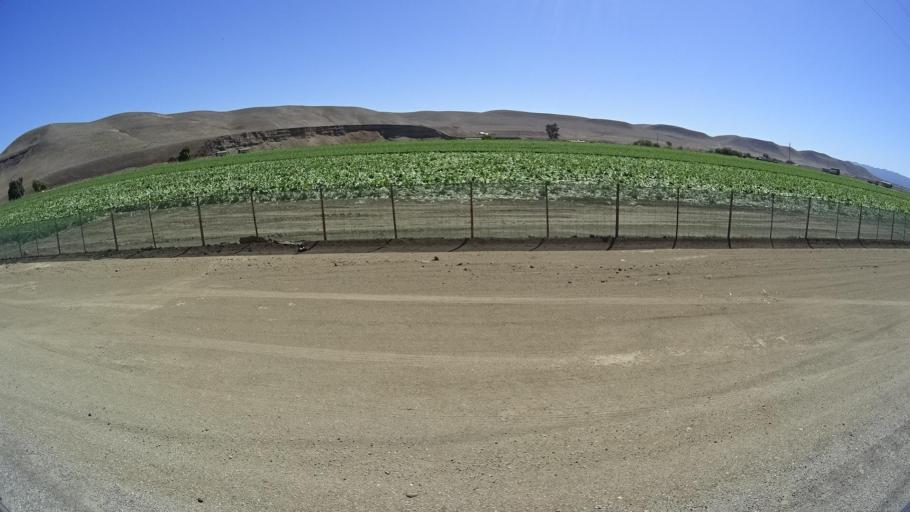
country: US
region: California
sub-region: Monterey County
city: King City
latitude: 36.2611
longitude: -121.0847
